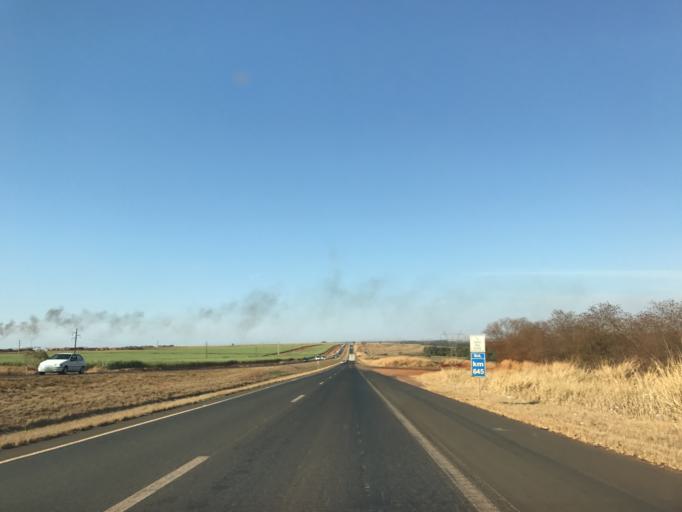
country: BR
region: Goias
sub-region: Goiatuba
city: Goiatuba
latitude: -17.9140
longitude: -49.2397
